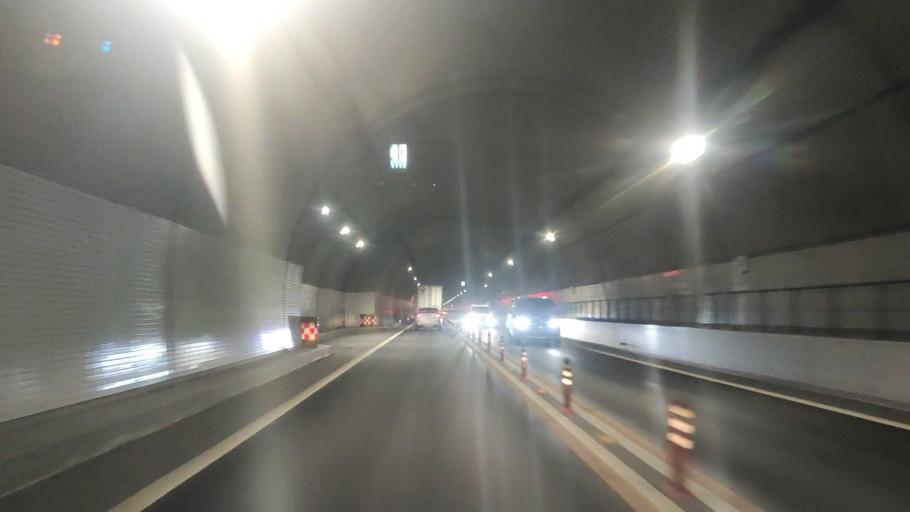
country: JP
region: Fukuoka
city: Yukuhashi
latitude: 33.7551
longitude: 130.9574
